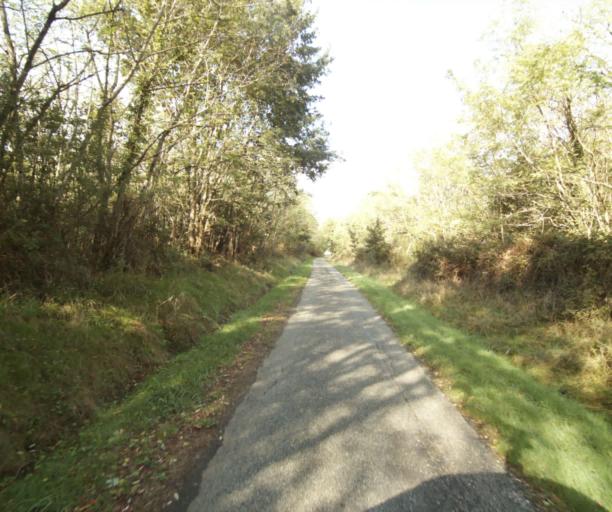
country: FR
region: Midi-Pyrenees
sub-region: Departement du Tarn-et-Garonne
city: Nohic
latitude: 43.9292
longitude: 1.4586
